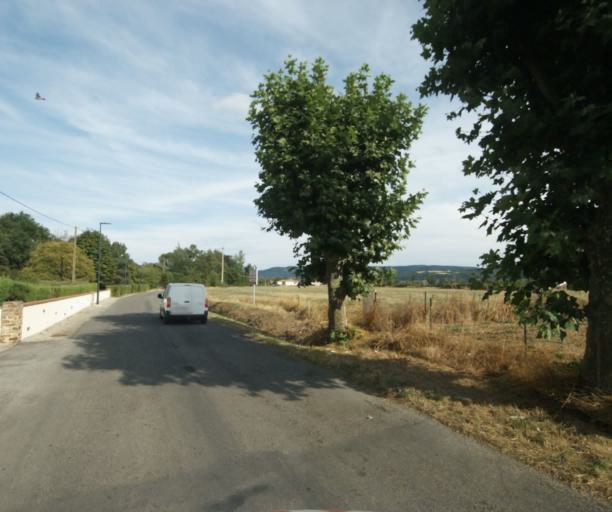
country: FR
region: Midi-Pyrenees
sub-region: Departement de la Haute-Garonne
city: Revel
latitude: 43.4713
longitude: 1.9945
